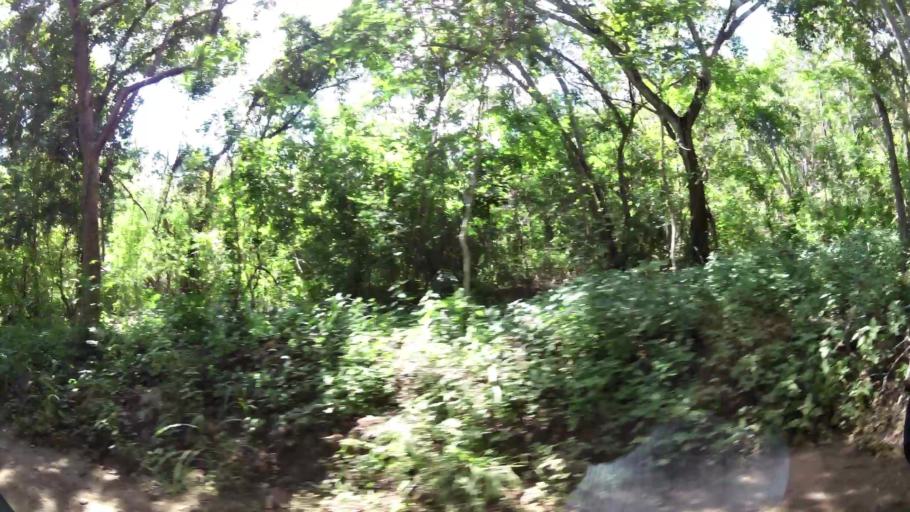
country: CR
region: Guanacaste
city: Bagaces
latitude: 10.5309
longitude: -85.2922
